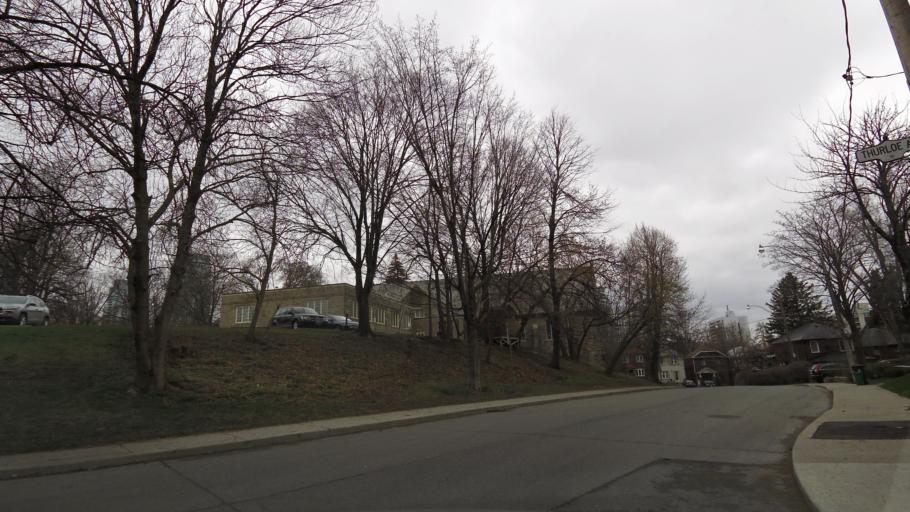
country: CA
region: Ontario
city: Toronto
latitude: 43.7030
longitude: -79.3907
